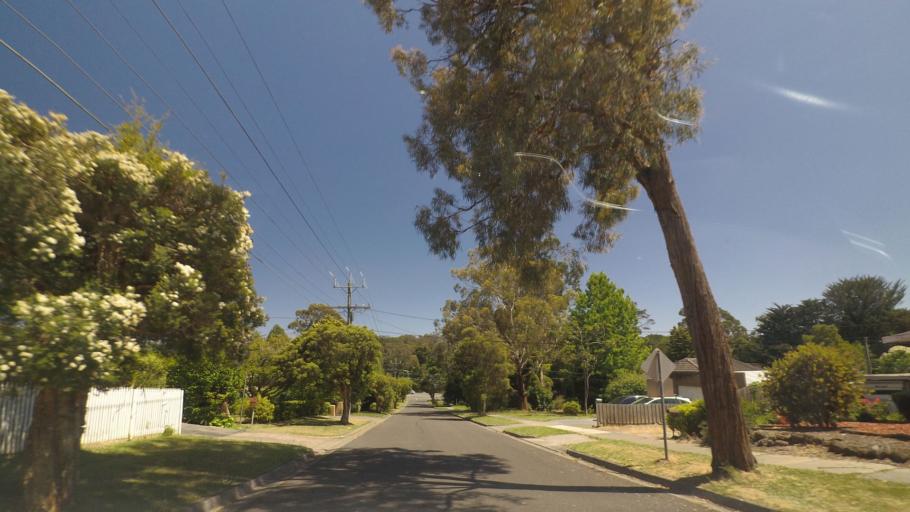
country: AU
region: Victoria
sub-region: Yarra Ranges
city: Montrose
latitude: -37.8077
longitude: 145.3529
